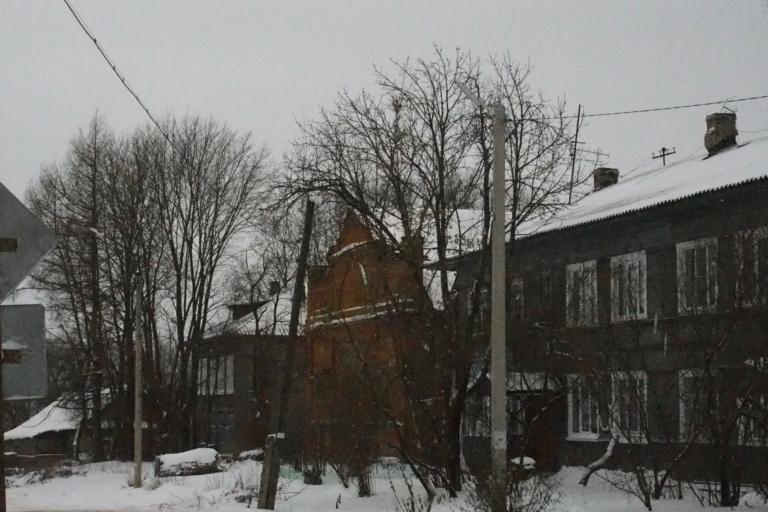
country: RU
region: Tverskaya
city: Bezhetsk
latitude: 57.7824
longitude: 36.6881
